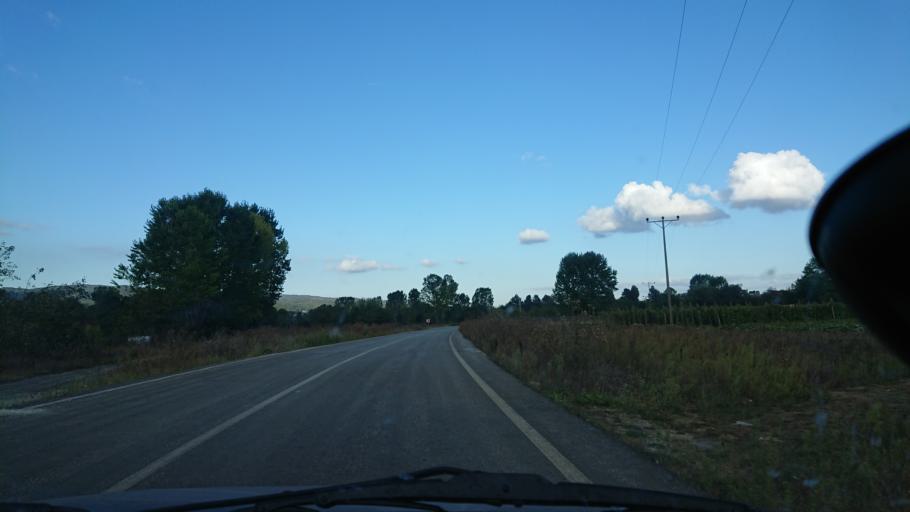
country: TR
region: Bilecik
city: Pazaryeri
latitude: 40.0133
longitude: 29.8247
